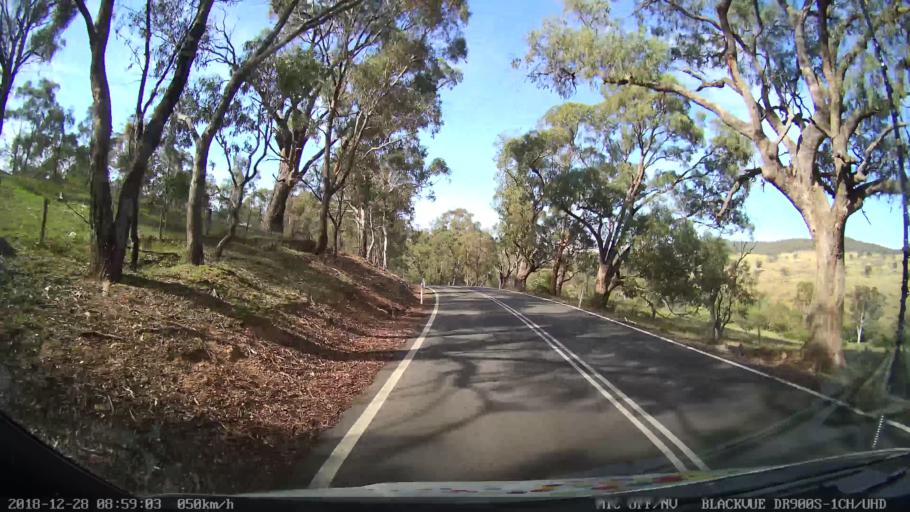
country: AU
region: New South Wales
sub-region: Upper Lachlan Shire
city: Crookwell
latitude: -34.1315
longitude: 149.3328
